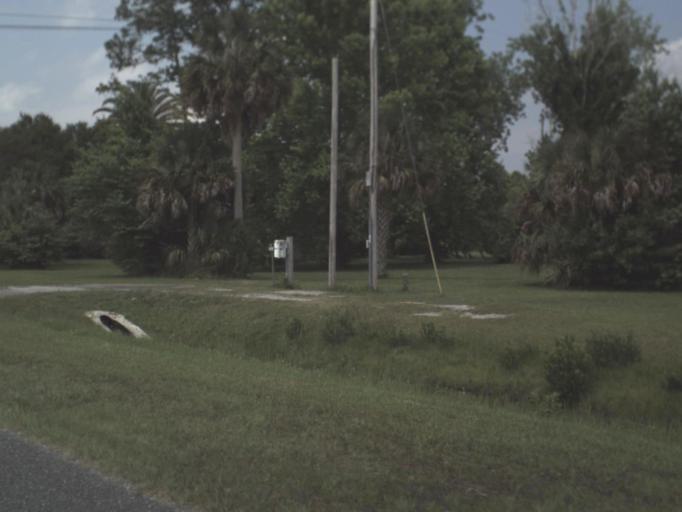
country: US
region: Florida
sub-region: Clay County
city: Green Cove Springs
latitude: 29.8234
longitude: -81.6606
